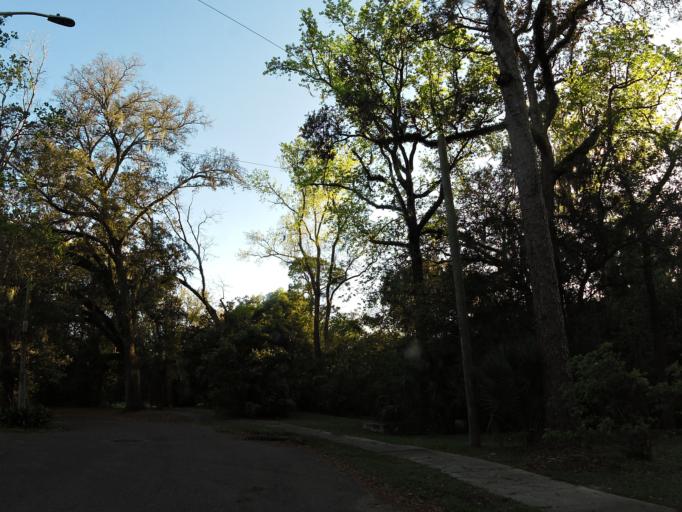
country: US
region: Florida
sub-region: Duval County
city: Jacksonville
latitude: 30.3360
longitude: -81.7031
